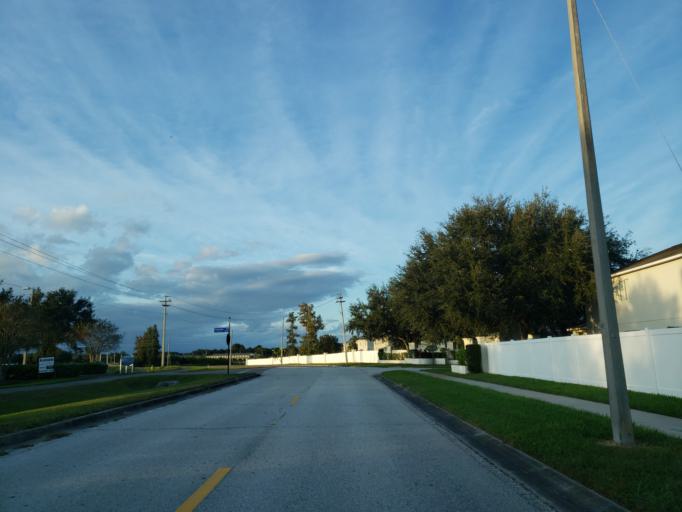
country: US
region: Florida
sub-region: Hillsborough County
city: Riverview
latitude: 27.7946
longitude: -82.3287
